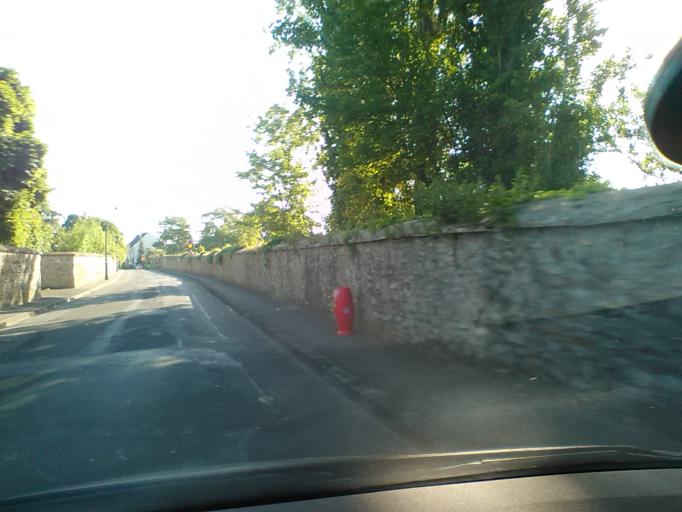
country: FR
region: Ile-de-France
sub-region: Departement de l'Essonne
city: Vert-le-Grand
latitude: 48.5686
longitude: 2.3588
